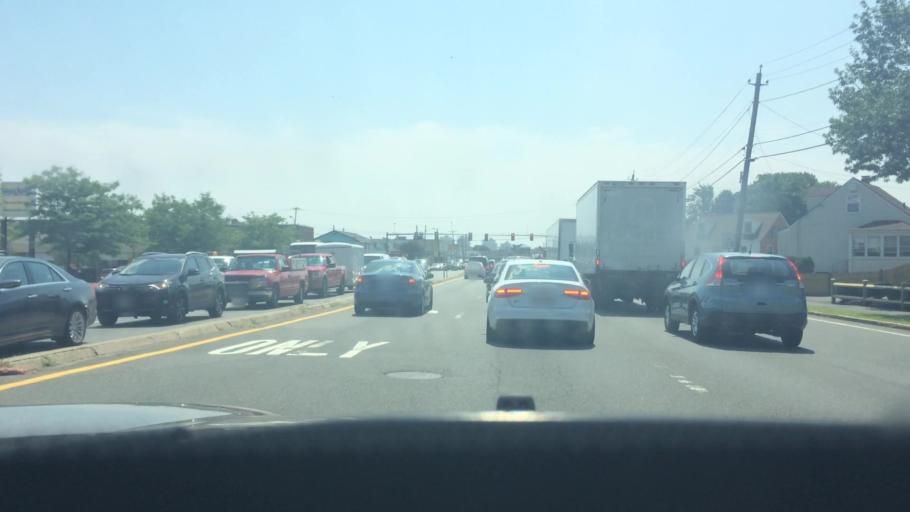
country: US
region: Massachusetts
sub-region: Suffolk County
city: Revere
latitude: 42.4260
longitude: -71.0125
